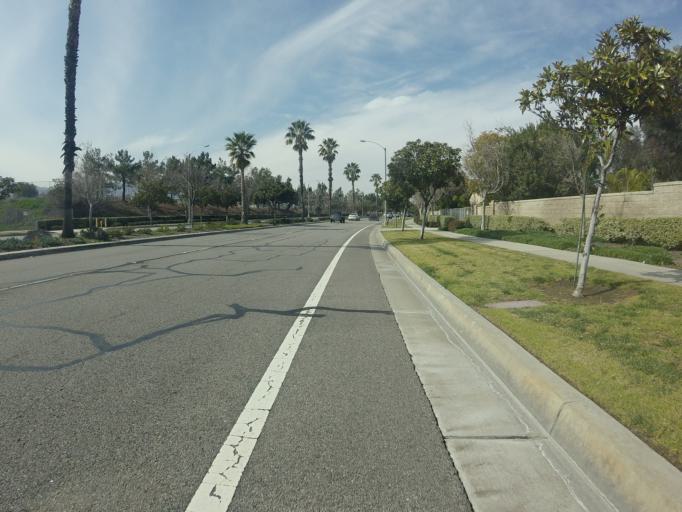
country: US
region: California
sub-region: Riverside County
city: Corona
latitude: 33.8390
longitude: -117.5677
